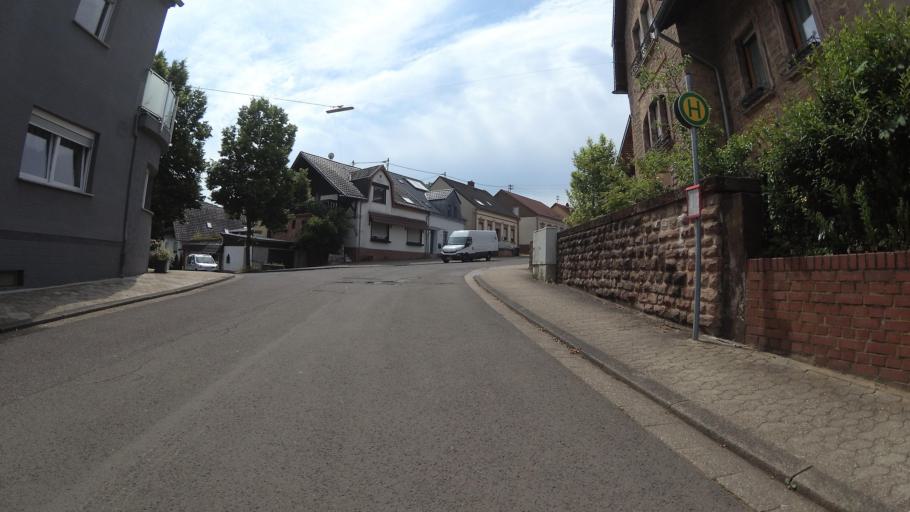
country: DE
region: Saarland
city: Quierschied
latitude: 49.3297
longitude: 7.0536
